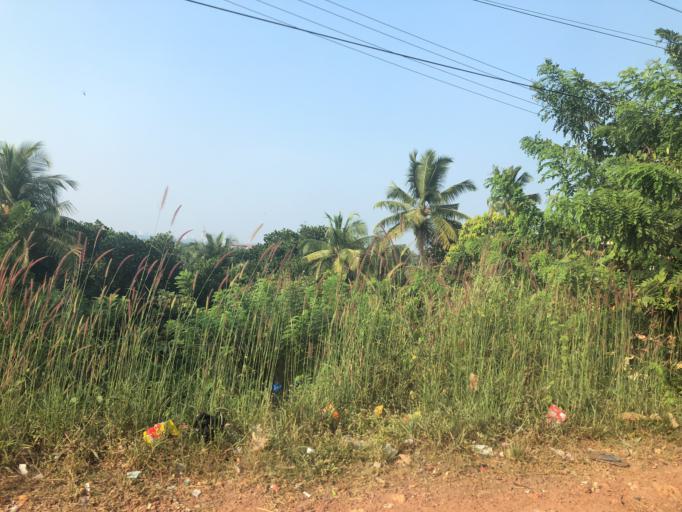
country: IN
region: Karnataka
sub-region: Dakshina Kannada
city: Ullal
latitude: 12.8190
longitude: 74.8622
